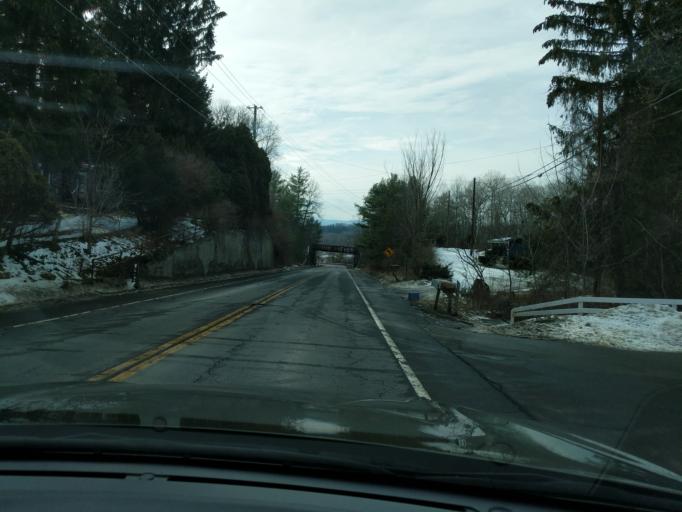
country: US
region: New York
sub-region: Tompkins County
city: Northeast Ithaca
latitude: 42.4593
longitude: -76.4304
